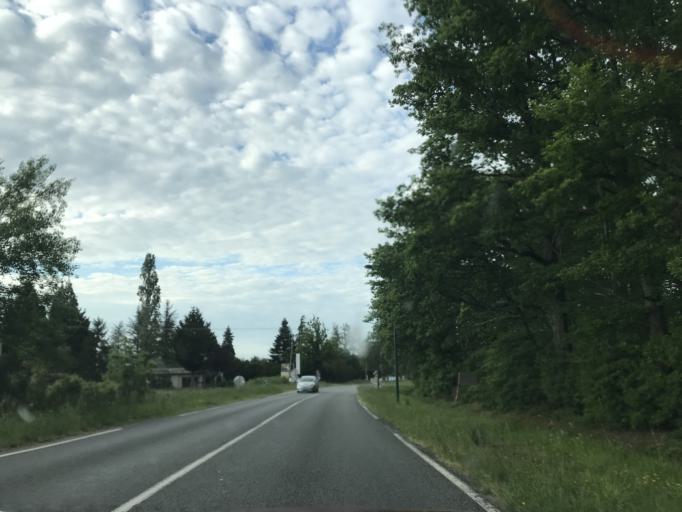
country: FR
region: Auvergne
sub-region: Departement de l'Allier
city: Brugheas
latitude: 46.0862
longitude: 3.3830
